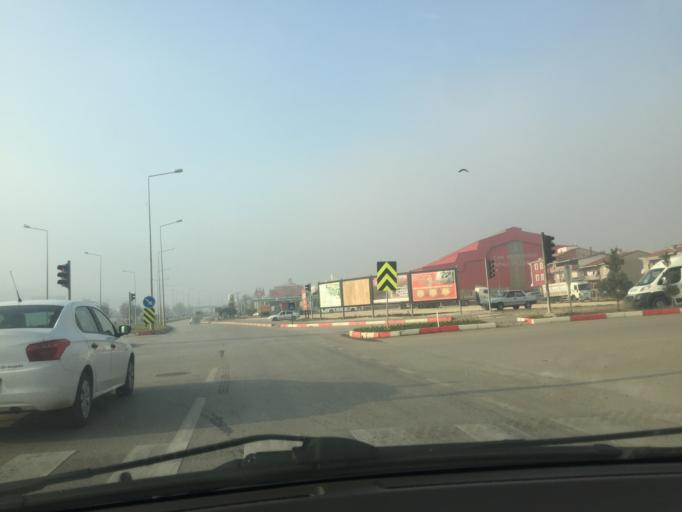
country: TR
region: Canakkale
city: Can
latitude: 40.0297
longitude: 27.0577
